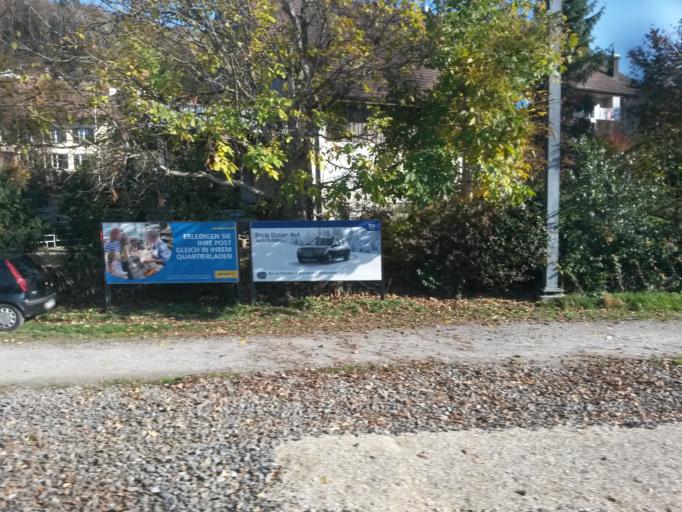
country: CH
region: Aargau
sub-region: Bezirk Kulm
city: Gontenschwil
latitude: 47.2726
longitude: 8.1680
